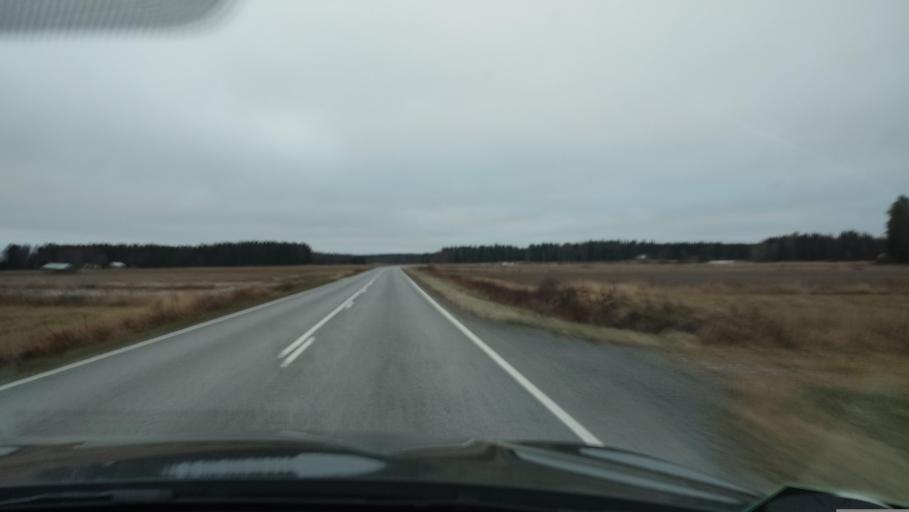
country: FI
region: Southern Ostrobothnia
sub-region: Suupohja
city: Karijoki
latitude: 62.3253
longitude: 21.8136
